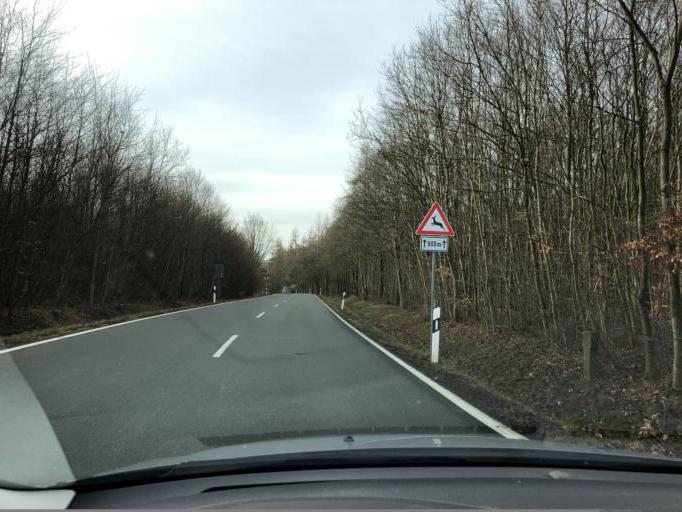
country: DE
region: Thuringia
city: Rastenberg
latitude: 51.1814
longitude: 11.4930
